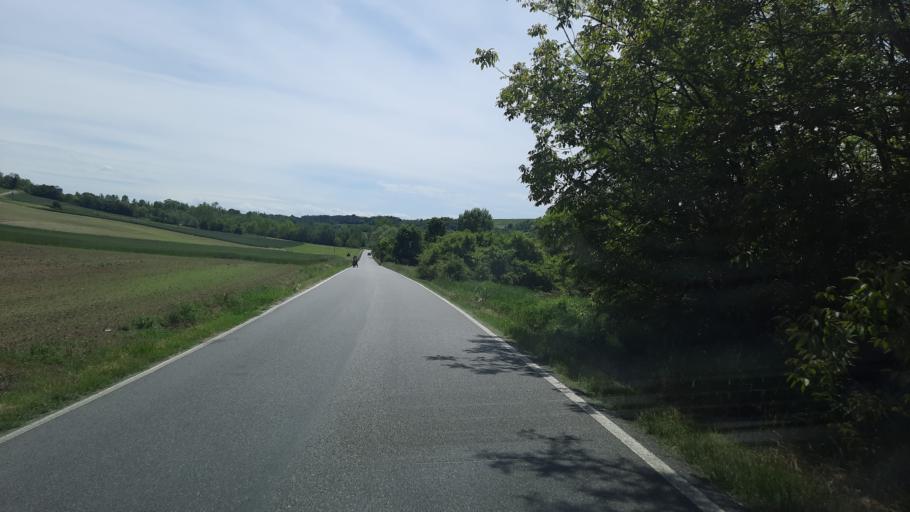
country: IT
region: Piedmont
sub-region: Provincia di Alessandria
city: Castelletto Merli
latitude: 45.0596
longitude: 8.2368
